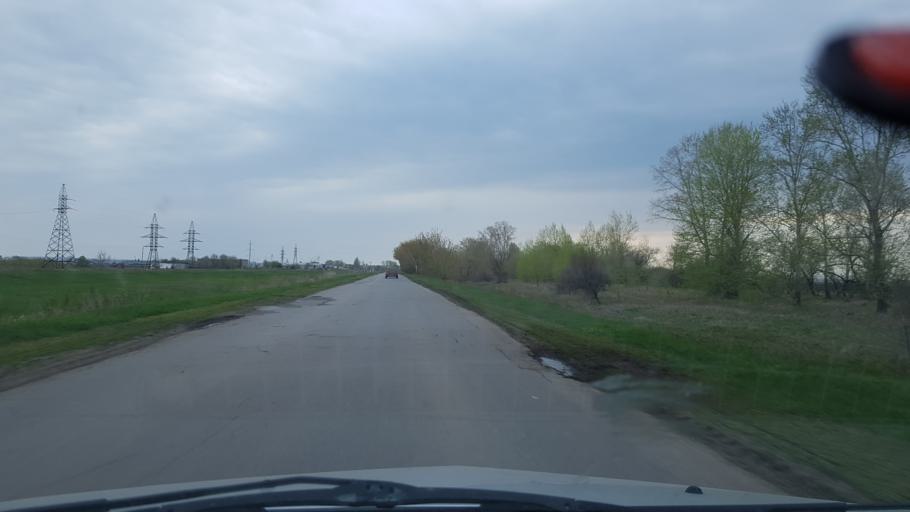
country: RU
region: Samara
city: Khryashchevka
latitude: 53.6716
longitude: 49.0964
